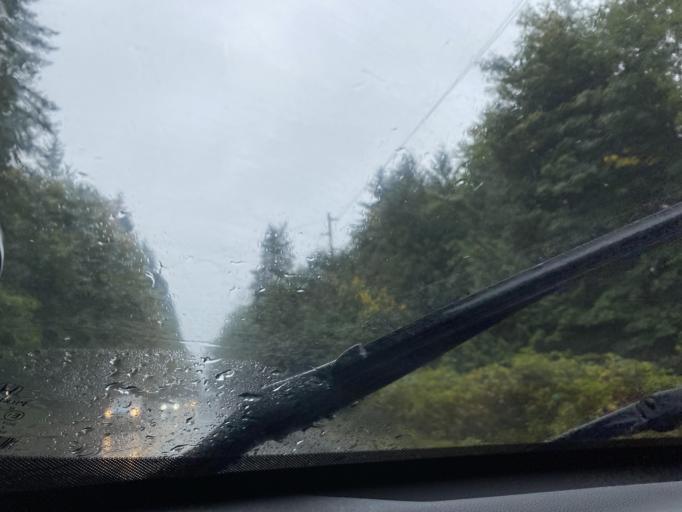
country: US
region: Washington
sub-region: Kitsap County
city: Suquamish
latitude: 47.6860
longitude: -122.5463
